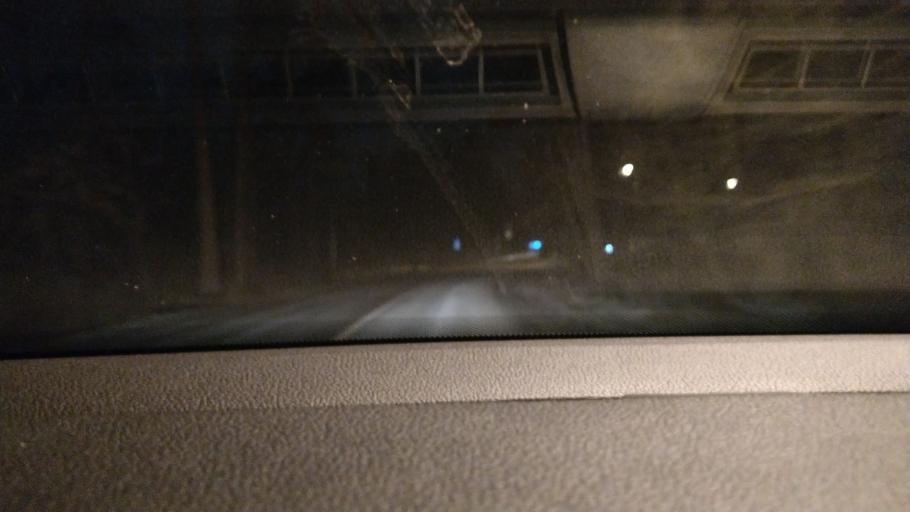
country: RU
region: Moskovskaya
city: Opalikha
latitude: 55.8025
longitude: 37.2694
